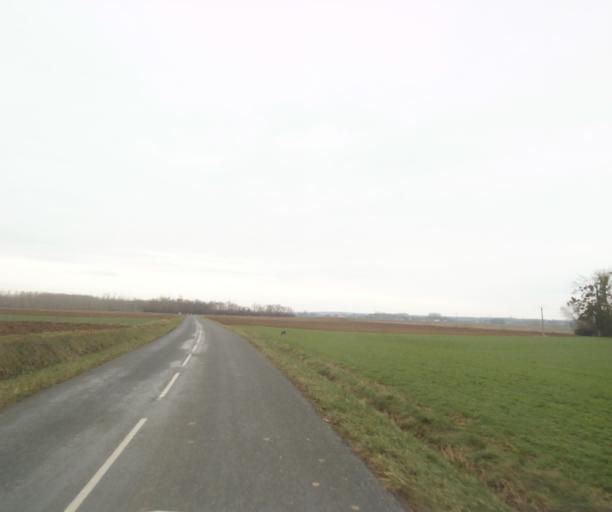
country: FR
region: Champagne-Ardenne
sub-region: Departement de la Haute-Marne
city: Villiers-en-Lieu
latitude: 48.6333
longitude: 4.7695
